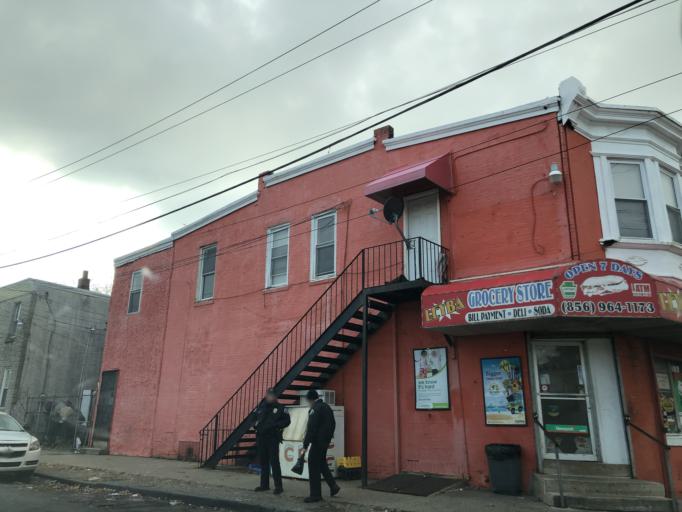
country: US
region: New Jersey
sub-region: Camden County
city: Camden
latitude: 39.9206
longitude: -75.1130
